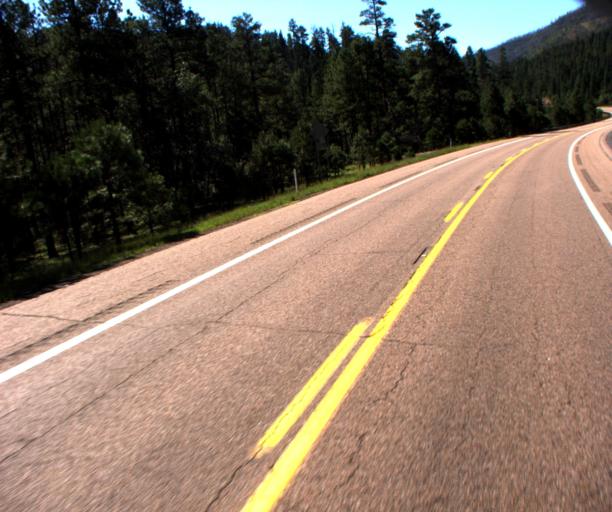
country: US
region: Arizona
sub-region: Apache County
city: Eagar
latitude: 33.9299
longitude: -109.1868
